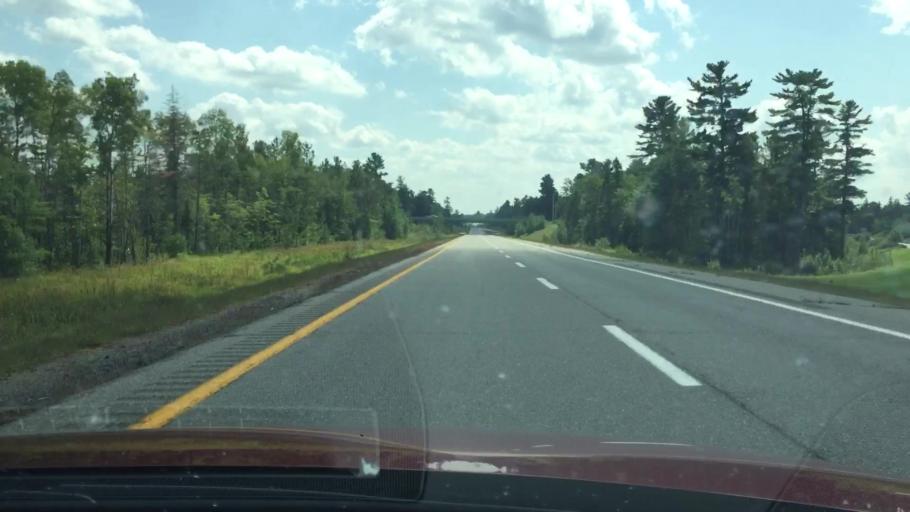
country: US
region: Maine
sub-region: Penobscot County
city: Lincoln
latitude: 45.3791
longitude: -68.6055
